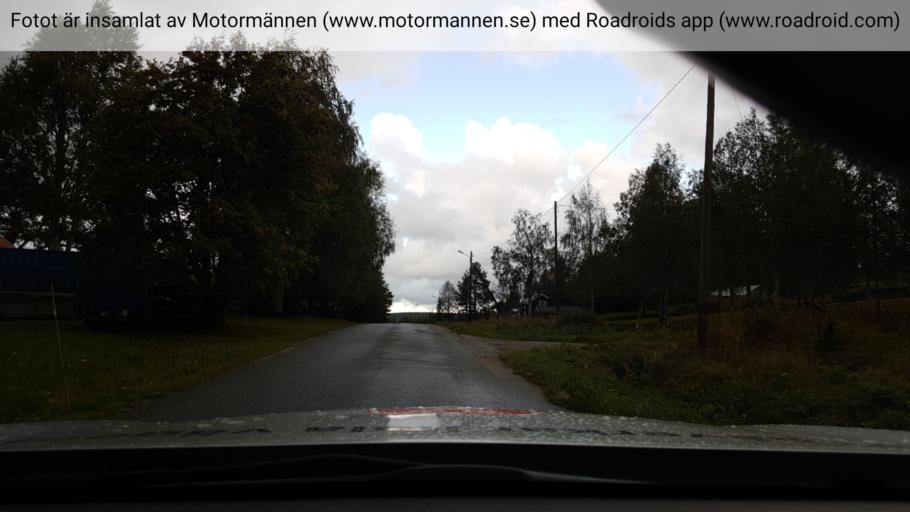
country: SE
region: Vaesterbotten
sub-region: Asele Kommun
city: Asele
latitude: 64.1892
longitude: 16.9179
